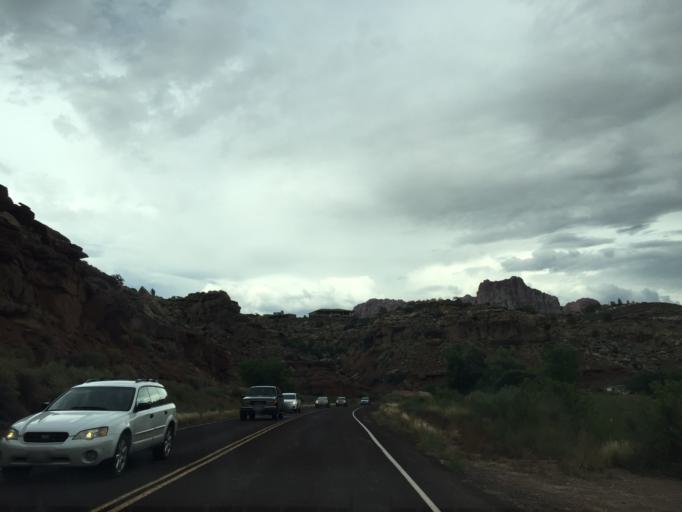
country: US
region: Utah
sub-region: Washington County
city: Hildale
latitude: 37.1622
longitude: -113.0265
